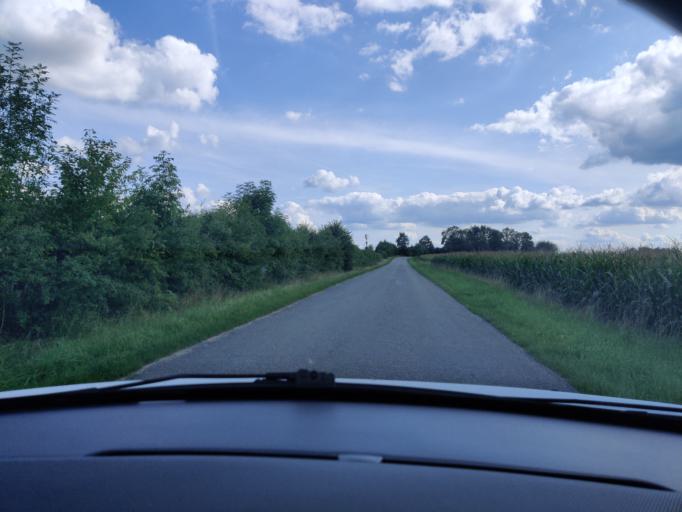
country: DE
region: Bavaria
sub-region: Upper Palatinate
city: Pfreimd
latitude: 49.4830
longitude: 12.1886
